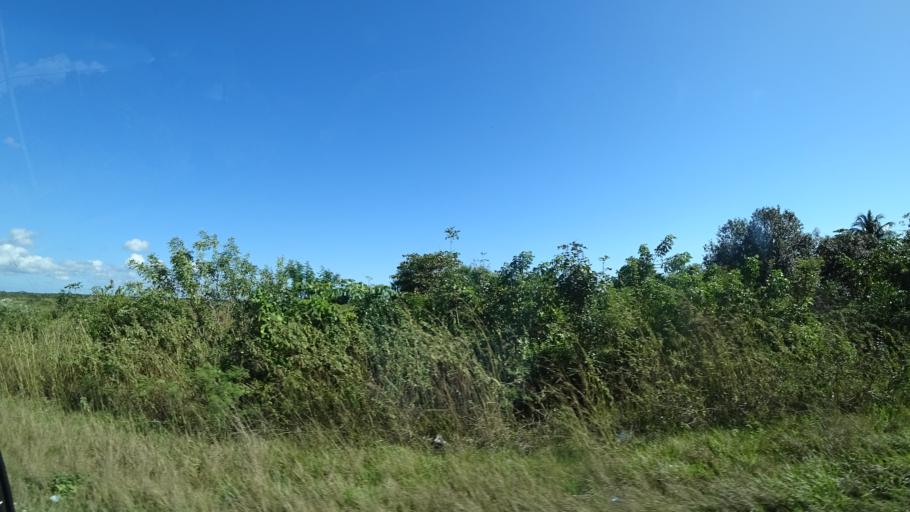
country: BZ
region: Belize
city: Belize City
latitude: 17.5834
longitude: -88.3451
